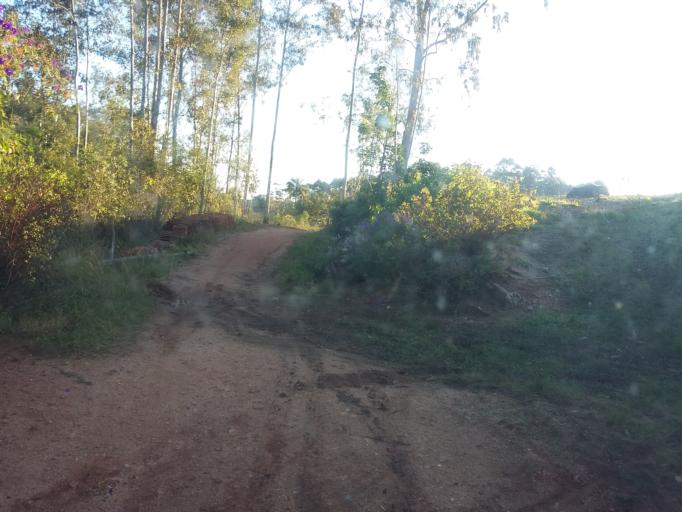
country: BR
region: Rio Grande do Sul
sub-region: Camaqua
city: Camaqua
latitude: -30.7040
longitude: -51.7645
